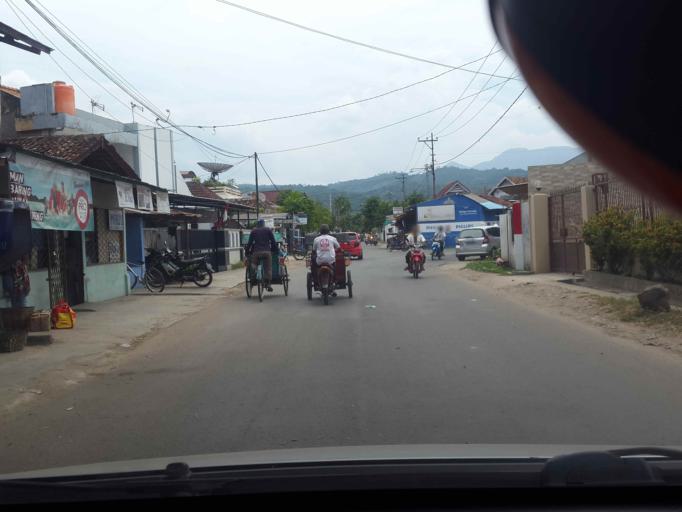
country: ID
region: Lampung
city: Bandarlampung
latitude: -5.4509
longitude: 105.2590
